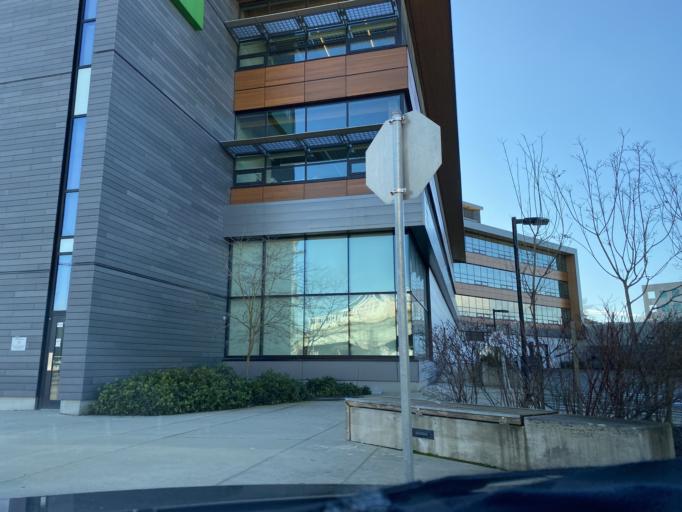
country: CA
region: British Columbia
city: Vancouver
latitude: 49.2661
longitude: -123.0814
